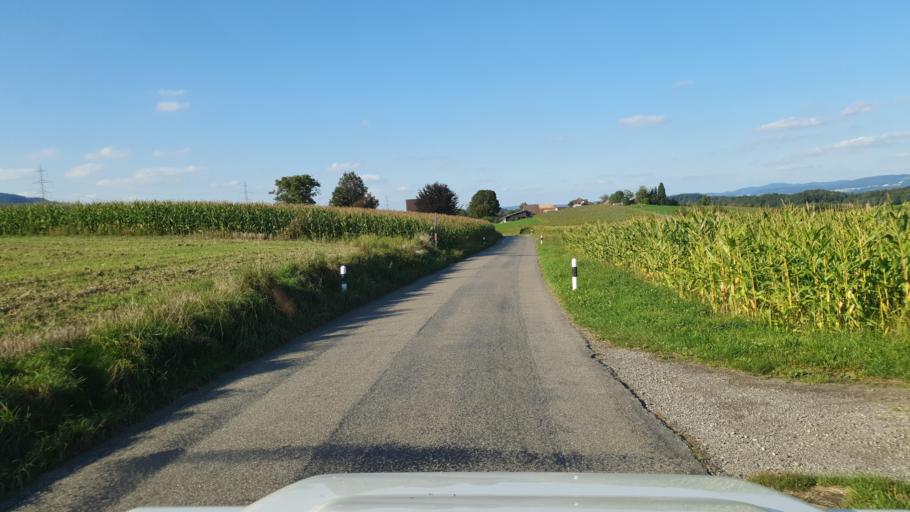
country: CH
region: Aargau
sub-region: Bezirk Muri
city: Oberruti
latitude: 47.1760
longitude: 8.3695
